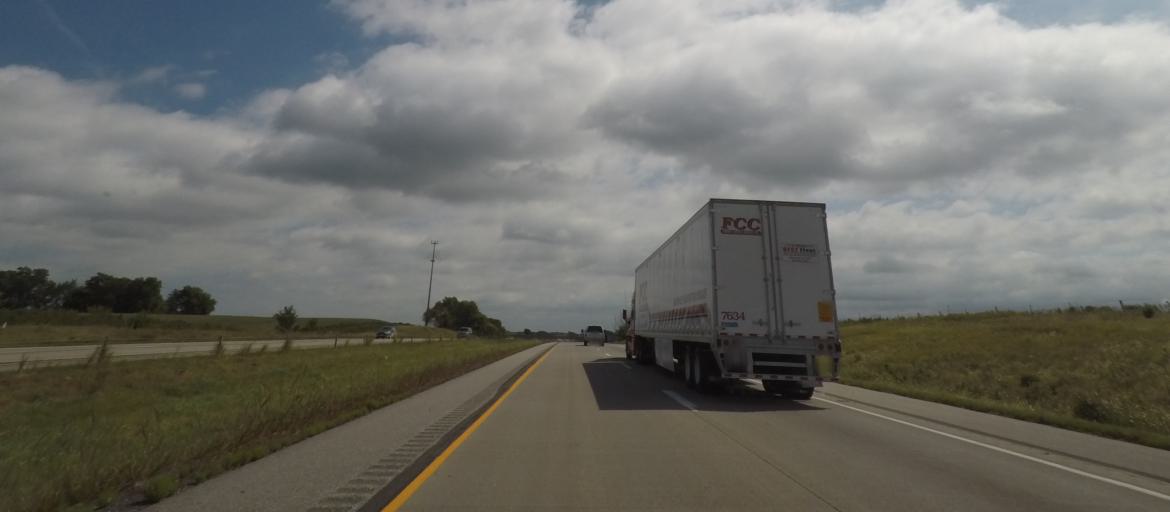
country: US
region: Iowa
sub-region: Jasper County
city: Newton
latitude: 41.6835
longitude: -93.1451
